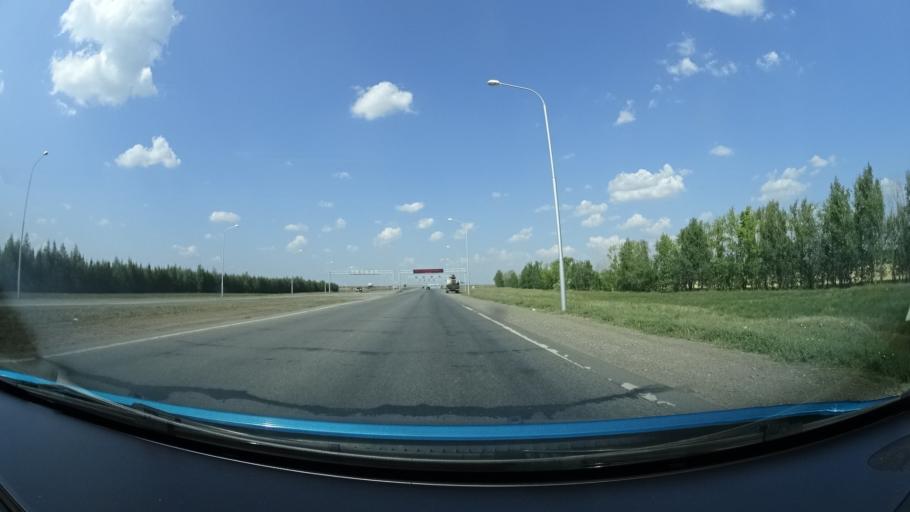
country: RU
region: Bashkortostan
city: Chishmy
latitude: 54.6668
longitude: 55.4121
